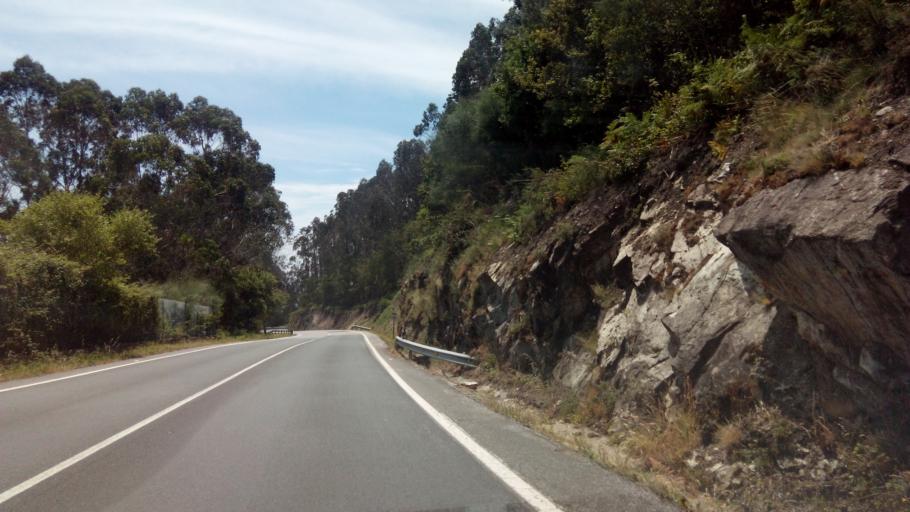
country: ES
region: Galicia
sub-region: Provincia de Pontevedra
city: Moana
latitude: 42.3209
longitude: -8.7231
